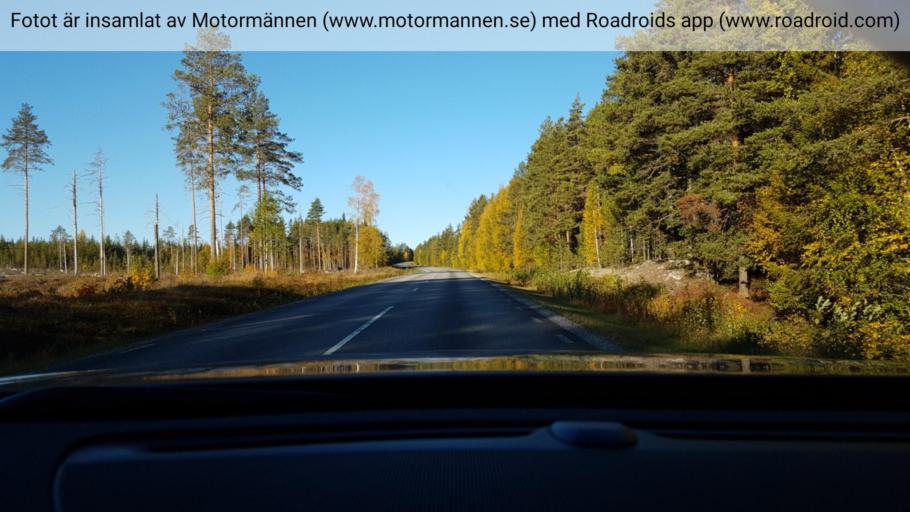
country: SE
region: Norrbotten
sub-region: Pitea Kommun
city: Roknas
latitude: 65.3395
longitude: 21.1673
